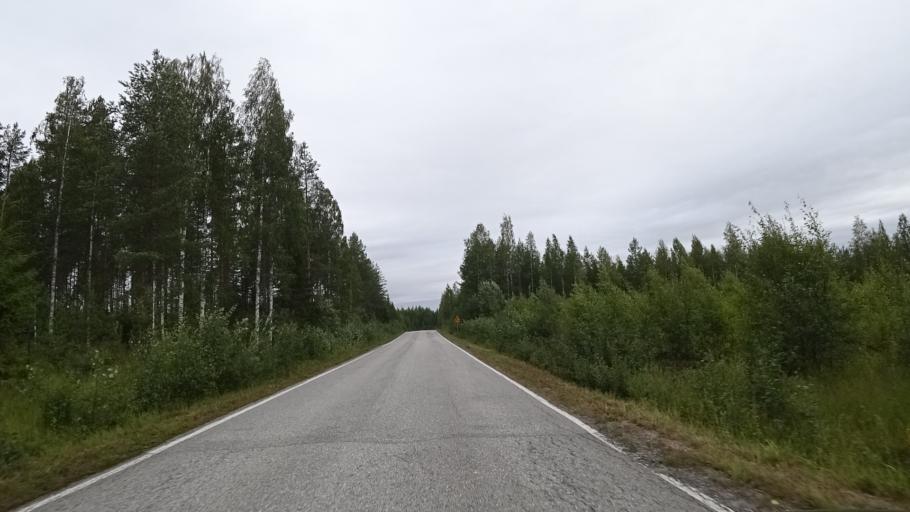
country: FI
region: North Karelia
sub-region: Pielisen Karjala
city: Lieksa
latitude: 63.3547
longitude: 30.2629
